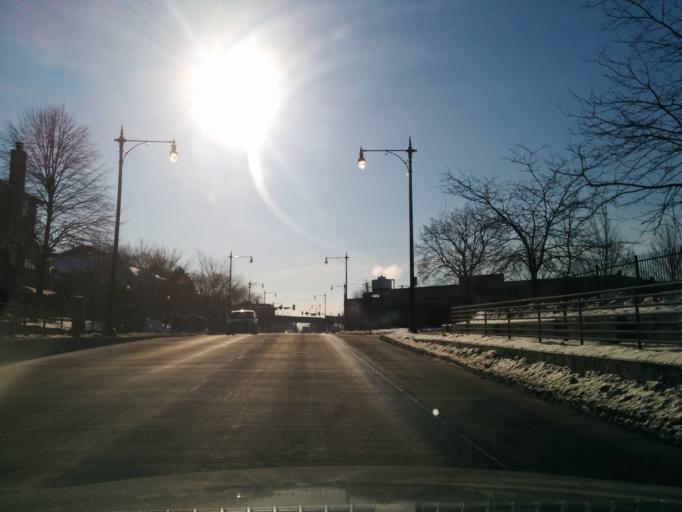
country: US
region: Illinois
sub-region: Cook County
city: Lincolnwood
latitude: 41.9502
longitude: -87.7422
